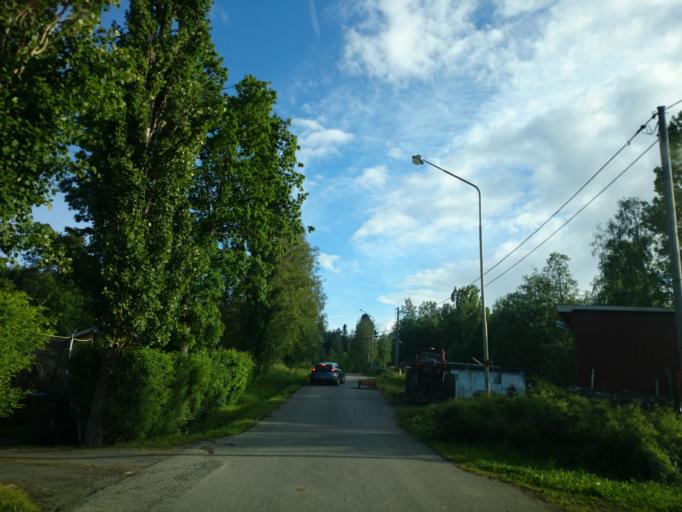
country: SE
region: Vaesternorrland
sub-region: Haernoesands Kommun
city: Haernoesand
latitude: 62.6098
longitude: 17.8839
